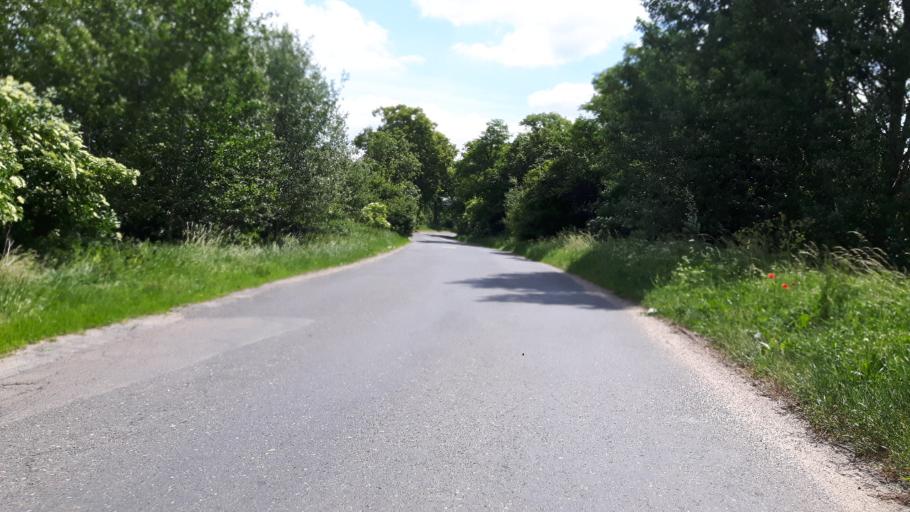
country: PL
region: Pomeranian Voivodeship
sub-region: Powiat gdanski
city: Cedry Wielkie
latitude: 54.3405
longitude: 18.7963
